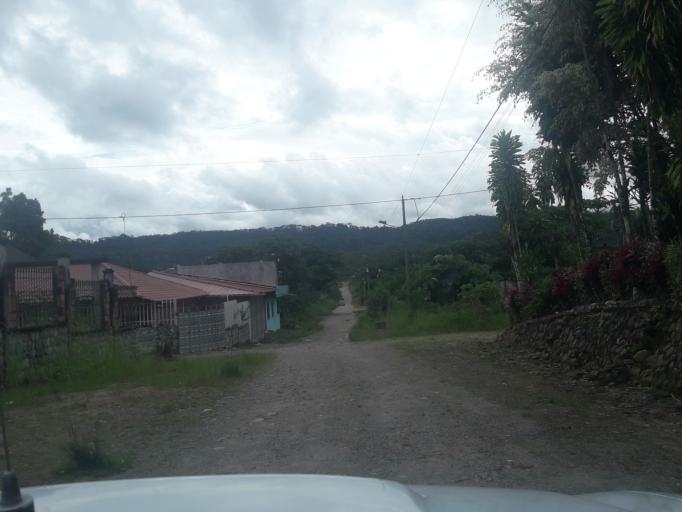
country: EC
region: Napo
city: Archidona
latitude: -0.9507
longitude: -77.8124
